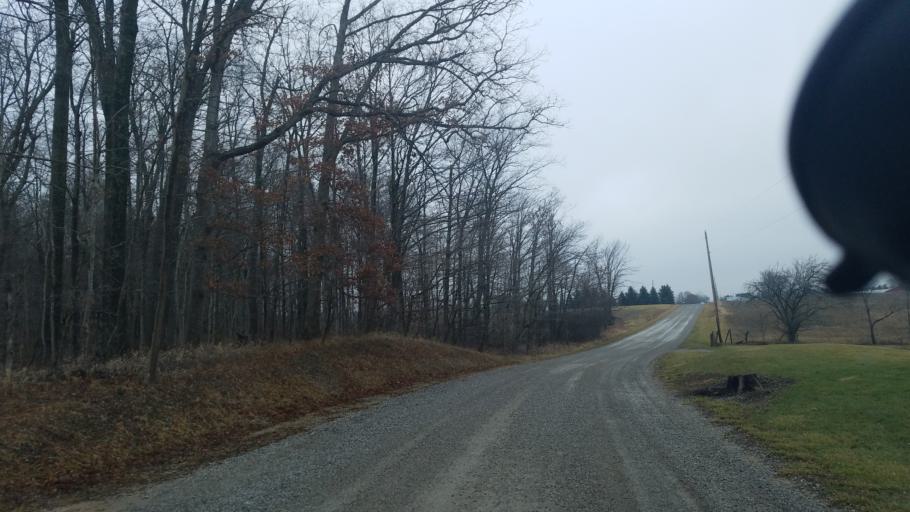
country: US
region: Ohio
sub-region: Morrow County
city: Mount Gilead
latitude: 40.5143
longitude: -82.7092
